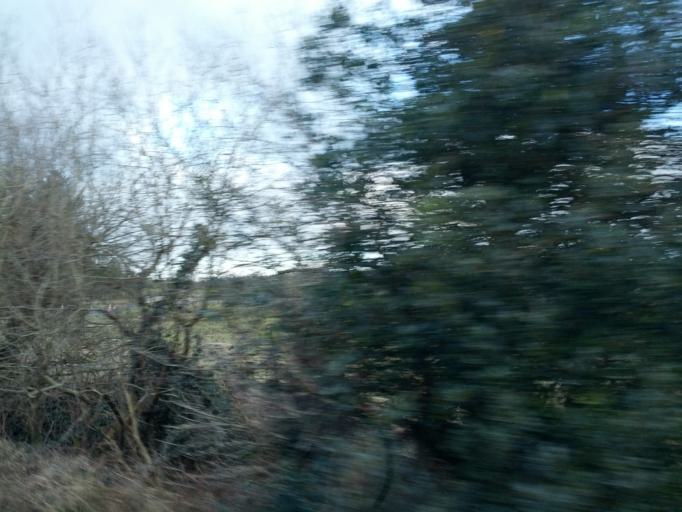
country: IE
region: Connaught
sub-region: County Galway
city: Athenry
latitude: 53.3586
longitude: -8.6705
